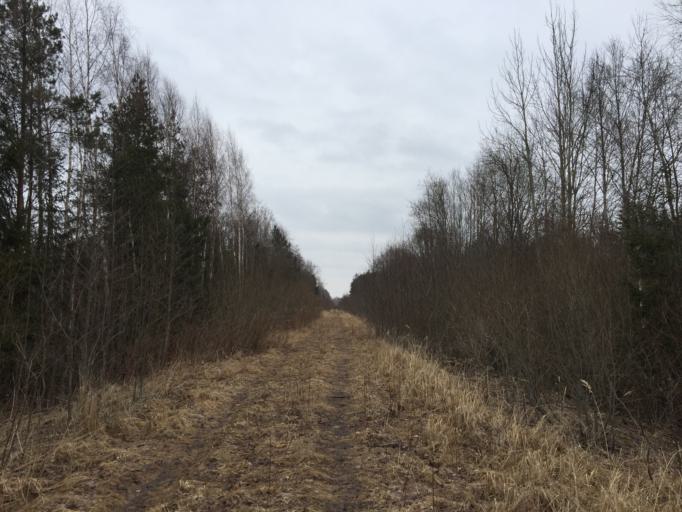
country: LV
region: Lielvarde
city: Lielvarde
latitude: 56.7586
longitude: 24.8176
